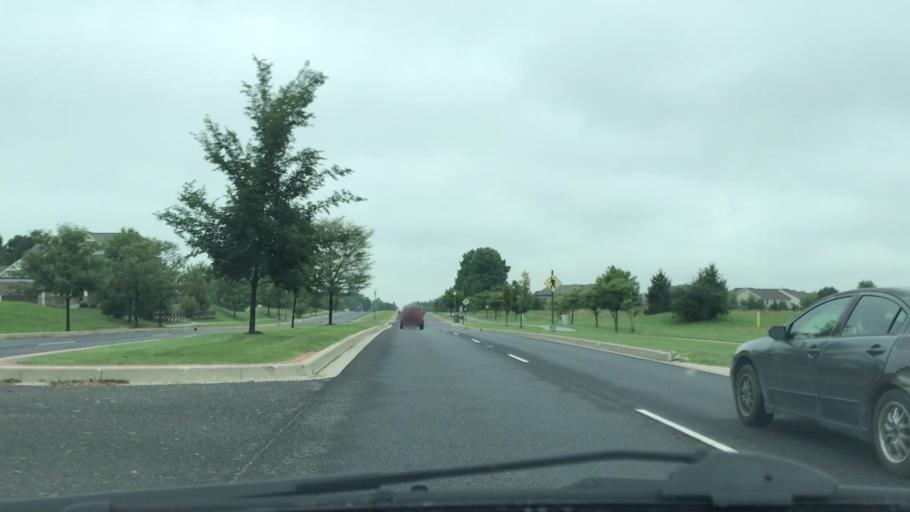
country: US
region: Indiana
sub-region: Hamilton County
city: Westfield
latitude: 40.0552
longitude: -86.0713
